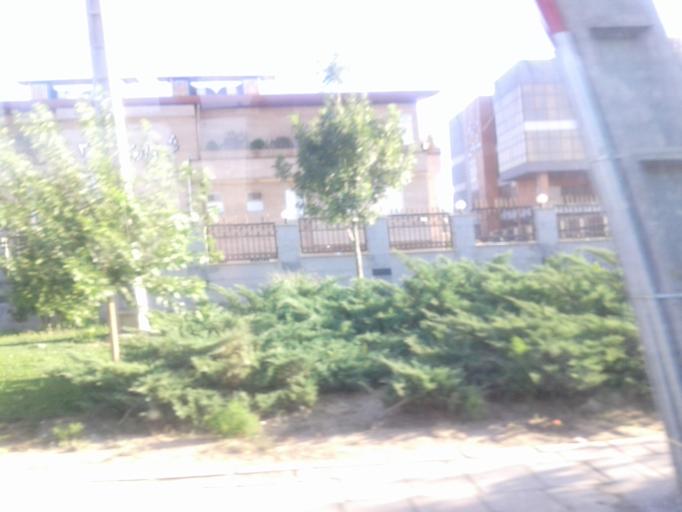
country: IR
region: Tehran
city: Rey
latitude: 35.6148
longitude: 51.3435
